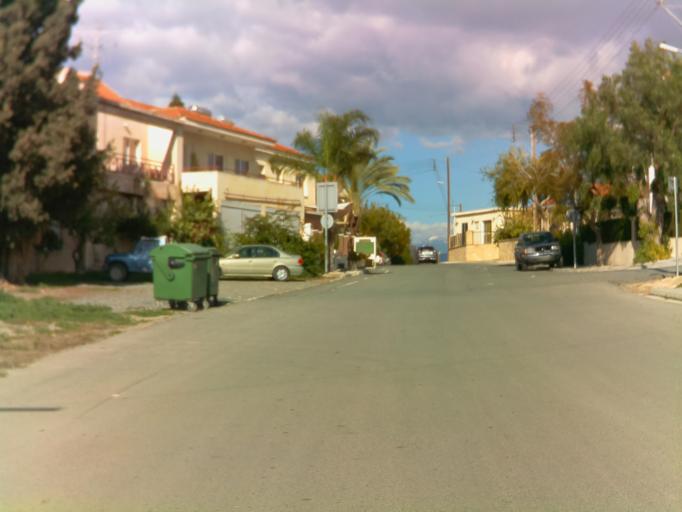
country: CY
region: Limassol
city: Pissouri
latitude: 34.6660
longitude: 32.6980
